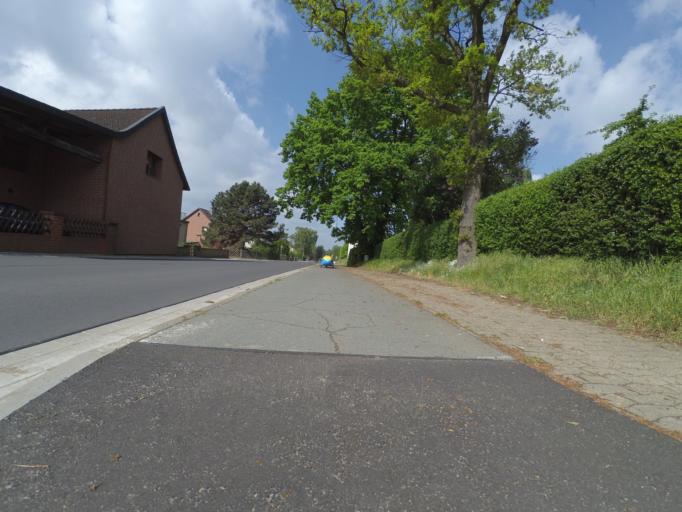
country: DE
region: Lower Saxony
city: Edemissen
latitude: 52.3872
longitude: 10.2352
